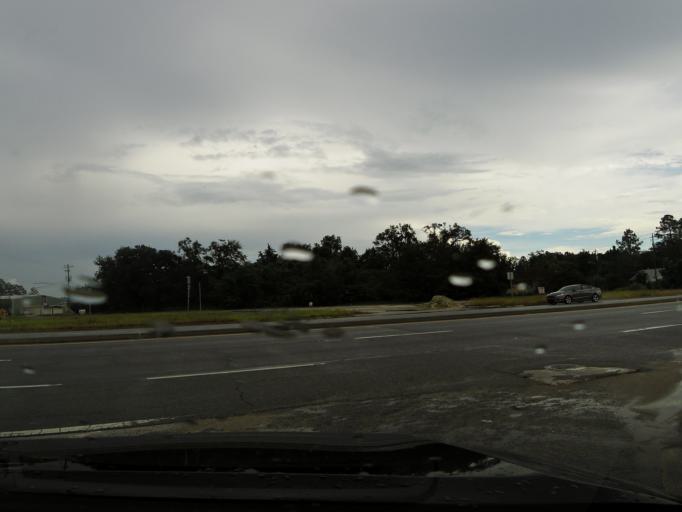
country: US
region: Georgia
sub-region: Wayne County
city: Jesup
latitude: 31.5943
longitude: -81.8707
